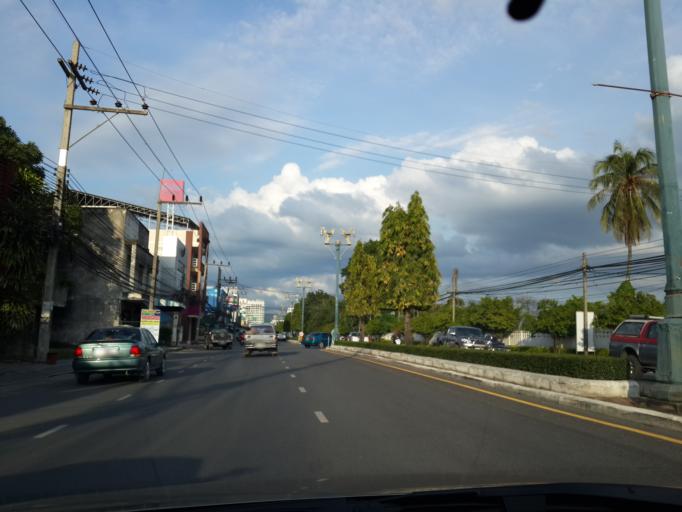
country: TH
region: Yala
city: Yala
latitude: 6.5501
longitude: 101.2789
